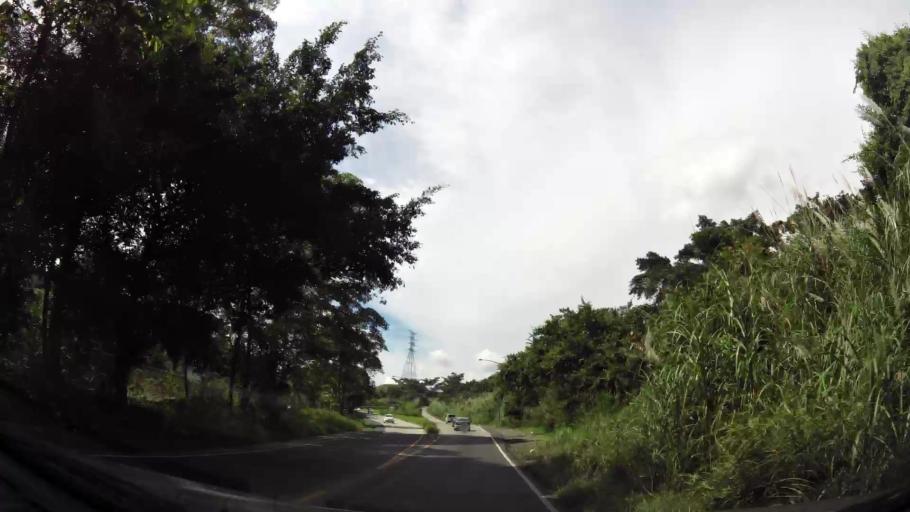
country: PA
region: Panama
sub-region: Distrito de Panama
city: Paraiso
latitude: 9.0346
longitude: -79.6259
